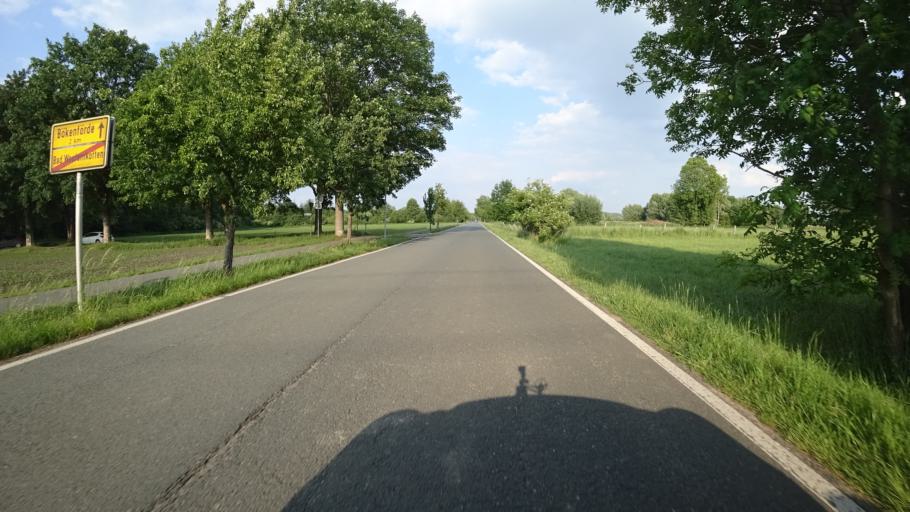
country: DE
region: North Rhine-Westphalia
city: Erwitte
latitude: 51.6322
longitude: 8.3741
